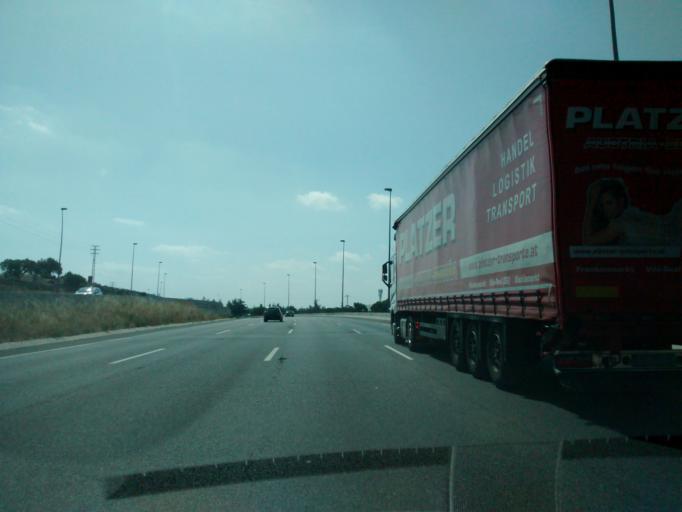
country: ES
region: Madrid
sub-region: Provincia de Madrid
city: Collado-Villalba
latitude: 40.6078
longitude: -3.9734
